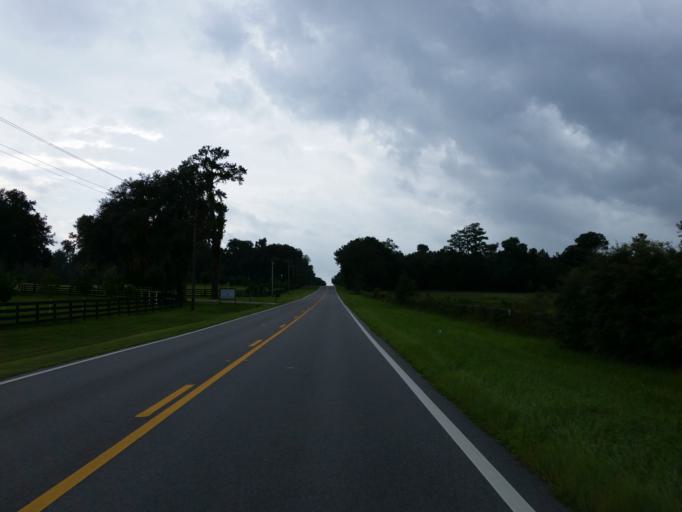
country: US
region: Florida
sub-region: Levy County
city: Williston
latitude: 29.4053
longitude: -82.3317
